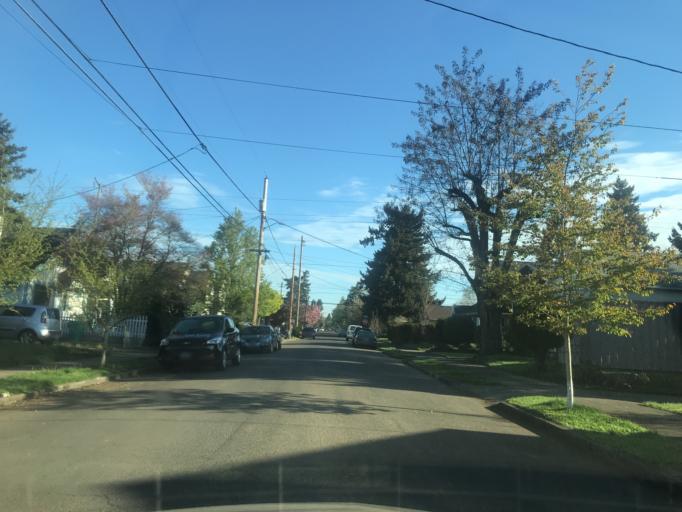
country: US
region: Oregon
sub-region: Multnomah County
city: Lents
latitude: 45.4892
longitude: -122.5881
